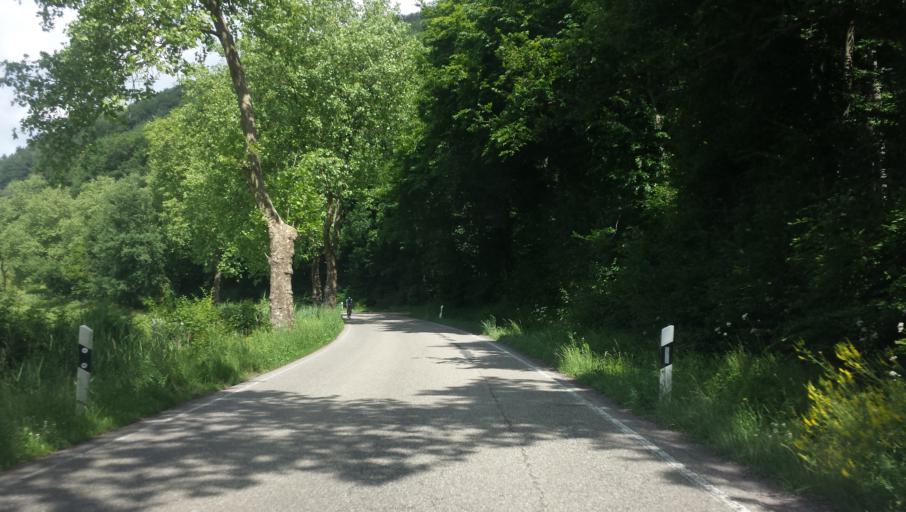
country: DE
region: Rheinland-Pfalz
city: Dernbach
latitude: 49.2389
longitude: 7.9875
